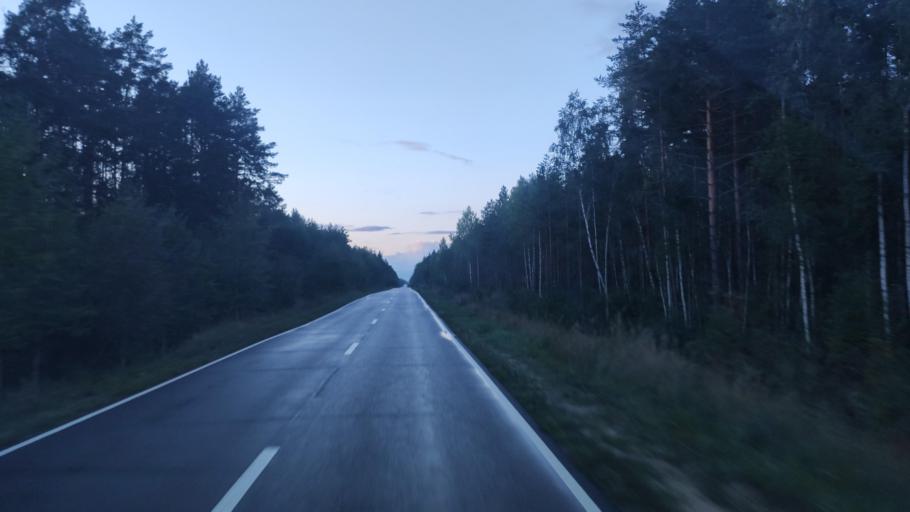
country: RU
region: Vladimir
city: Galitsy
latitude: 56.0745
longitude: 42.8673
